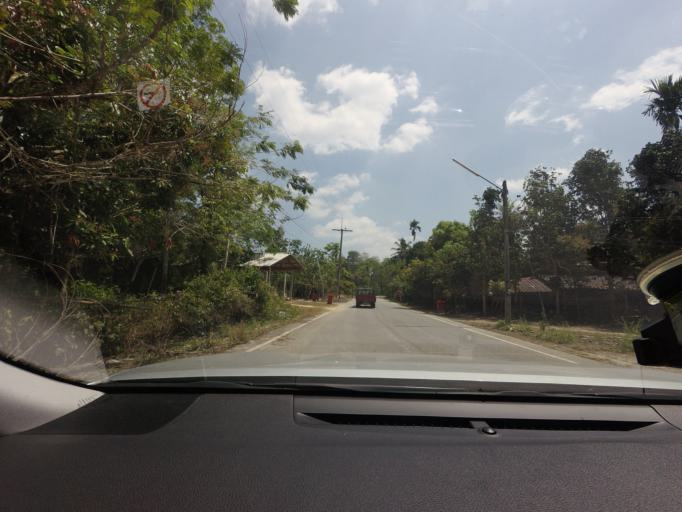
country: TH
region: Narathiwat
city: Rueso
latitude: 6.3889
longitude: 101.5059
